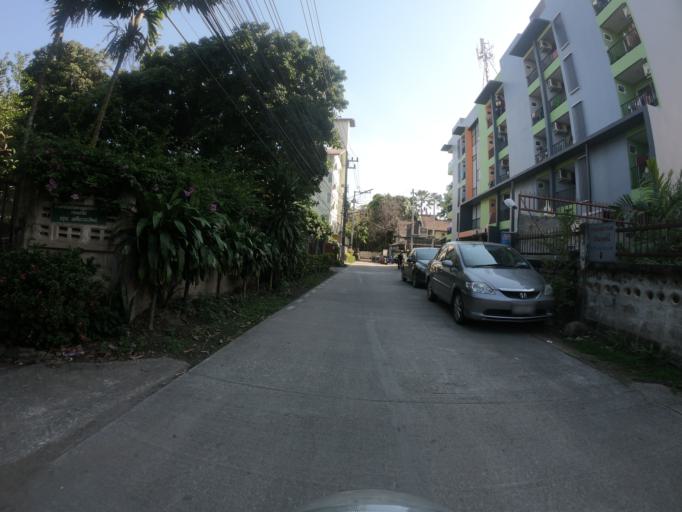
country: TH
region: Chiang Mai
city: Chiang Mai
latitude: 18.8072
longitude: 98.9800
